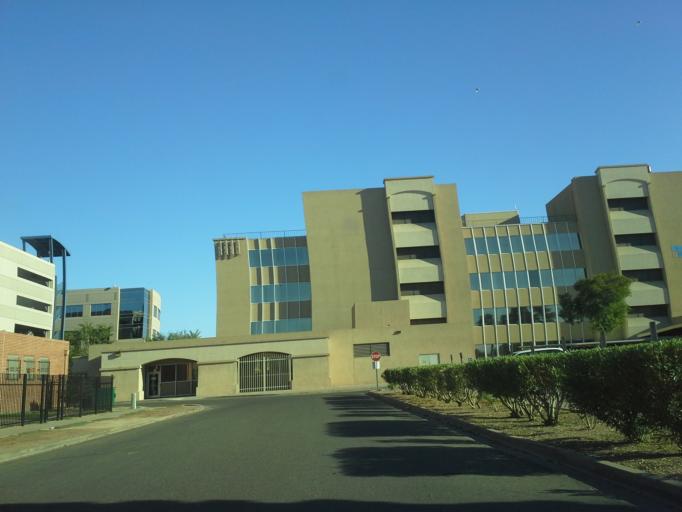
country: US
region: Arizona
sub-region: Maricopa County
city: Phoenix
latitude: 33.4503
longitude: -112.0936
